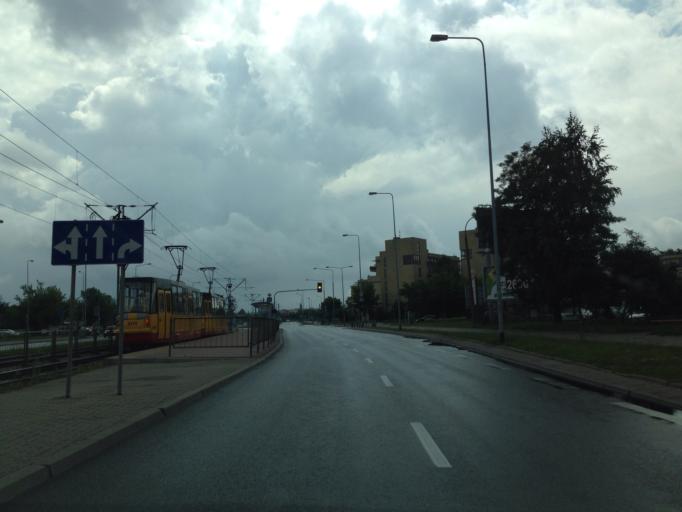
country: PL
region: Masovian Voivodeship
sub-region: Warszawa
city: Bemowo
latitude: 52.2494
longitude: 20.9193
